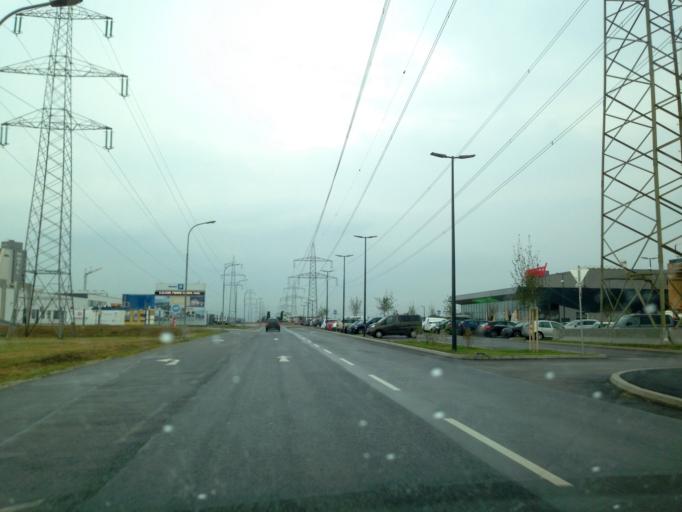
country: AT
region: Burgenland
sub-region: Politischer Bezirk Neusiedl am See
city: Parndorf
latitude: 47.9786
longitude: 16.8529
